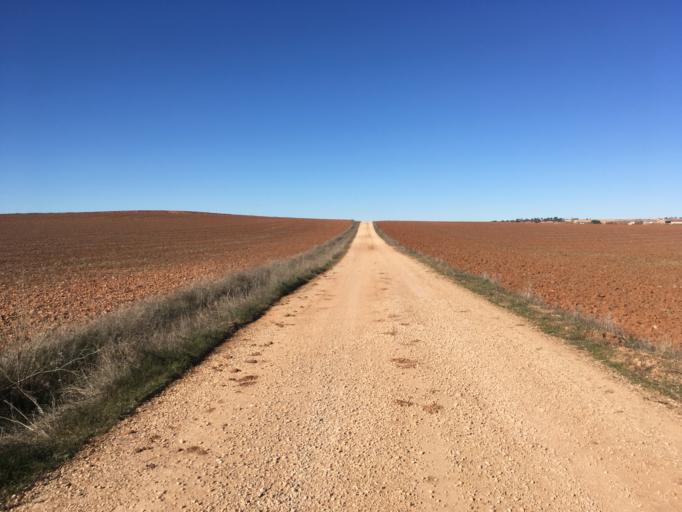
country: ES
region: Castille-La Mancha
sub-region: Provincia de Cuenca
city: Atalaya del Canavate
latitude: 39.5408
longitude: -2.2416
